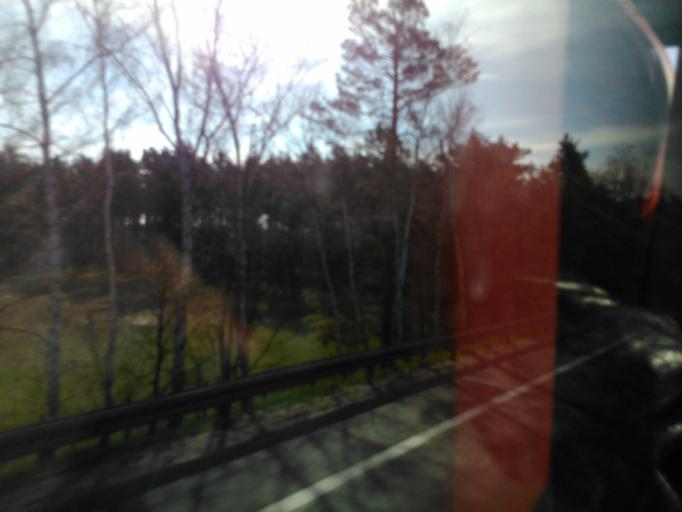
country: PL
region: Kujawsko-Pomorskie
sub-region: Powiat aleksandrowski
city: Aleksandrow Kujawski
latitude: 52.9108
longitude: 18.7189
